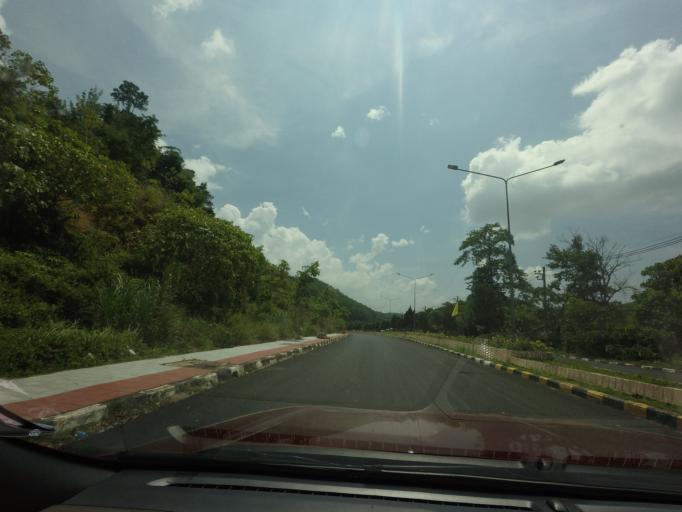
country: TH
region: Yala
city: Betong
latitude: 5.7535
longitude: 101.0439
